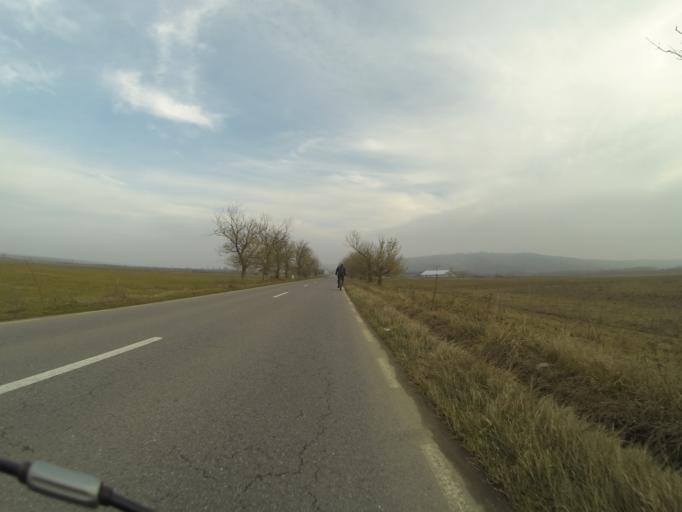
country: RO
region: Mehedinti
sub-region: Comuna Corlatel
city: Corlatel
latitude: 44.3990
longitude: 22.9199
